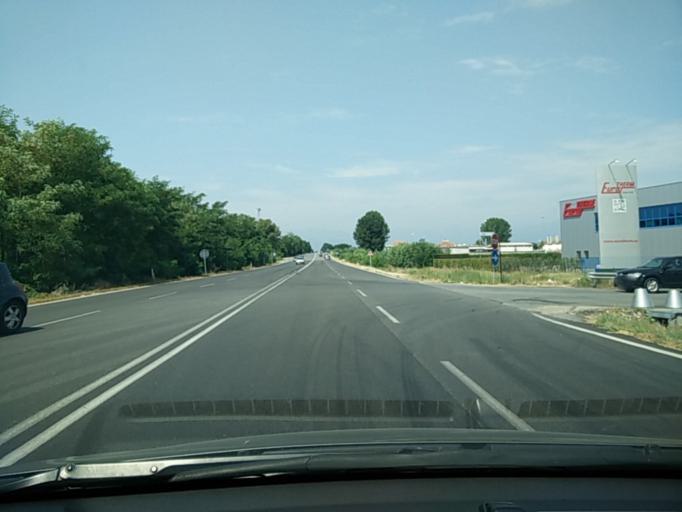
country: IT
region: Piedmont
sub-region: Provincia di Torino
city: Volpiano
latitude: 45.1846
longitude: 7.7905
